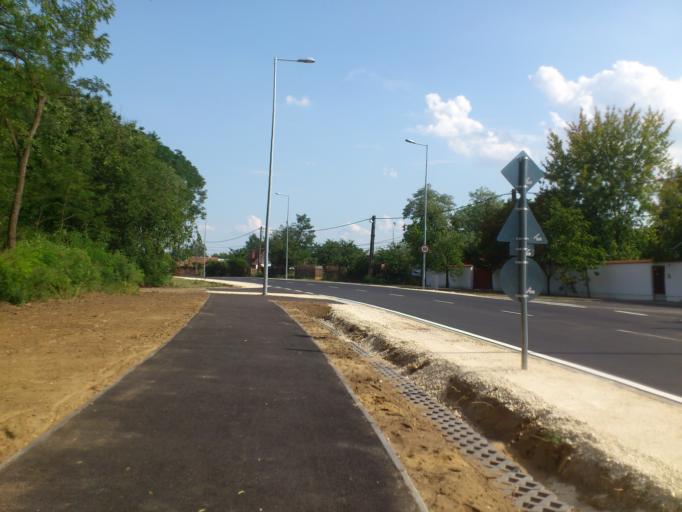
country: HU
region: Budapest
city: Budapest XVII. keruelet
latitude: 47.4517
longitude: 19.2313
